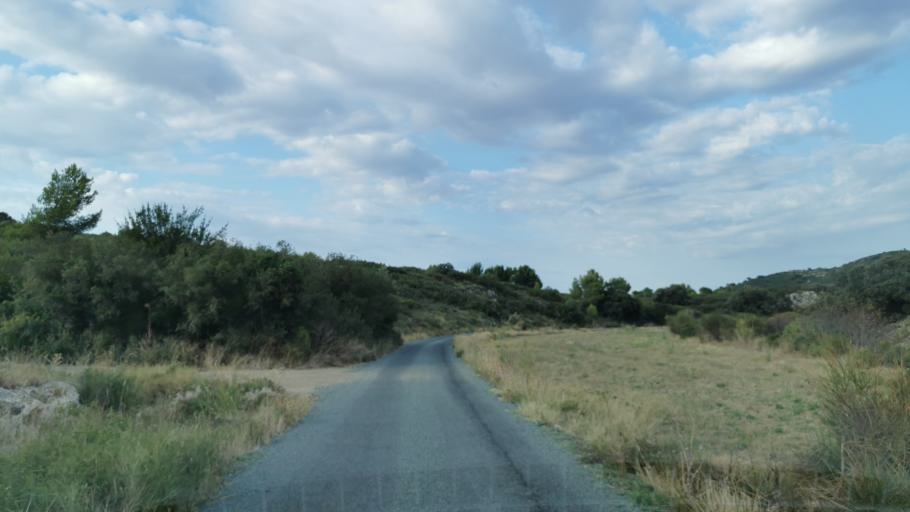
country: FR
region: Languedoc-Roussillon
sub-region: Departement de l'Aude
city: Nevian
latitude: 43.1902
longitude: 2.8919
